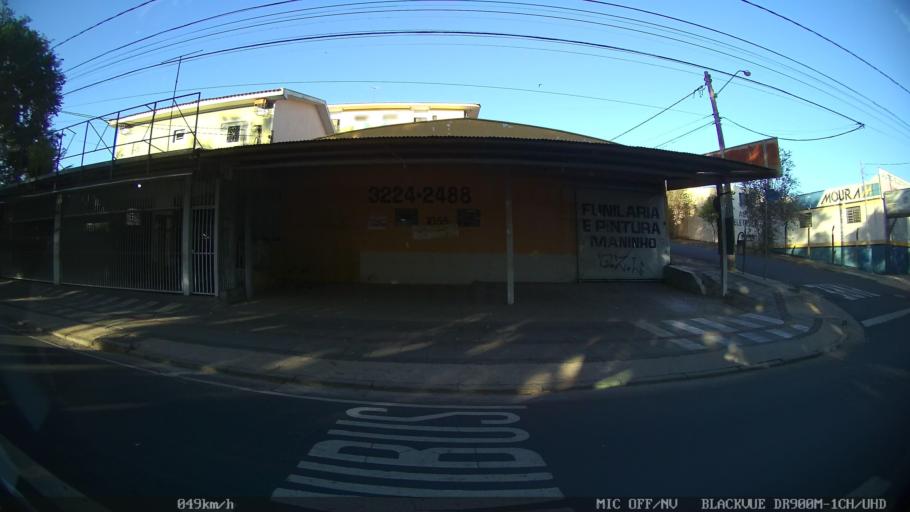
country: BR
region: Sao Paulo
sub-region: Sao Jose Do Rio Preto
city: Sao Jose do Rio Preto
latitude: -20.7901
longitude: -49.3761
